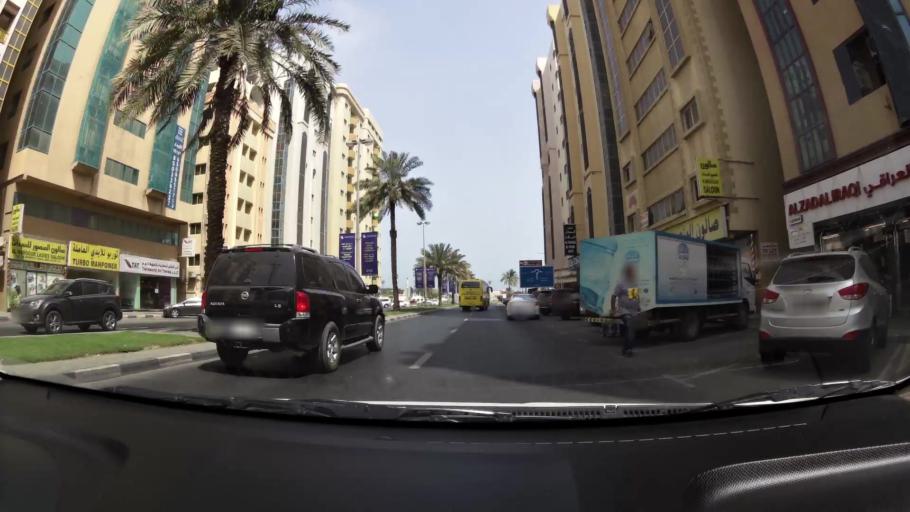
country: AE
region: Ash Shariqah
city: Sharjah
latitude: 25.3561
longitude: 55.3806
